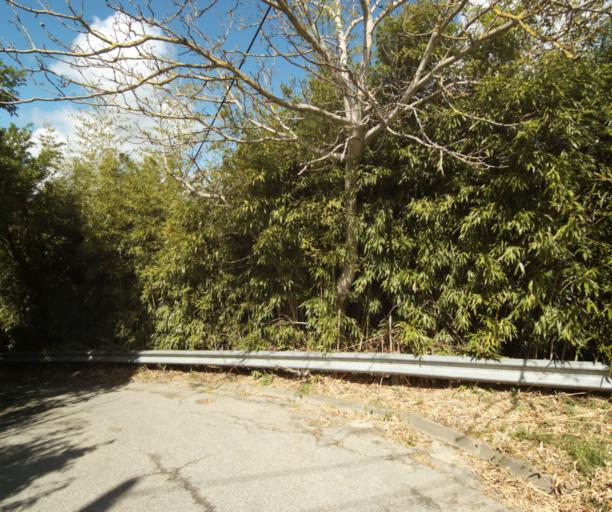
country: FR
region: Midi-Pyrenees
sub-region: Departement de l'Ariege
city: Saverdun
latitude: 43.2307
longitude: 1.5768
